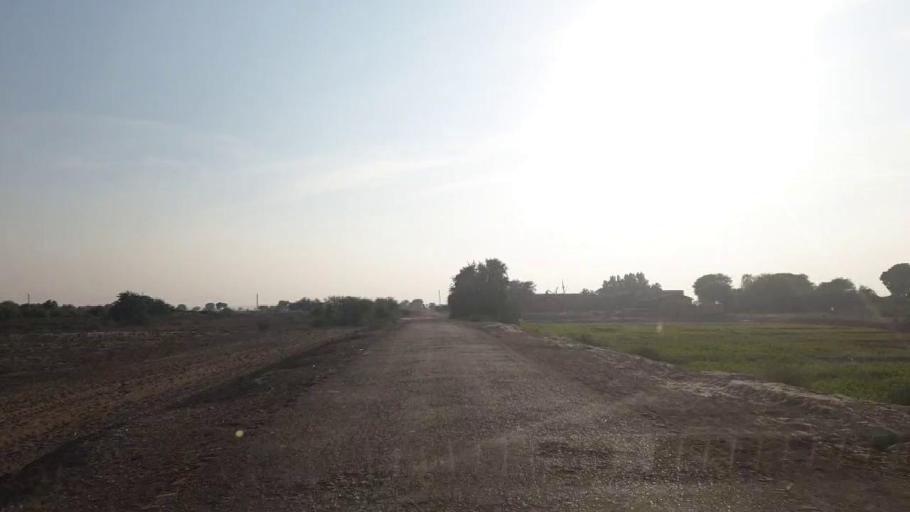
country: PK
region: Sindh
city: Sann
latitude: 25.9438
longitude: 68.1833
